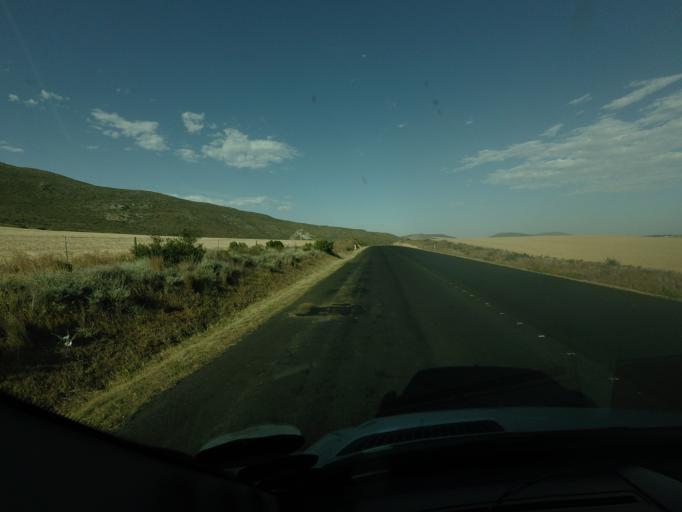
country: ZA
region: Western Cape
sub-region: Overberg District Municipality
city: Swellendam
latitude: -34.1002
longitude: 20.2072
